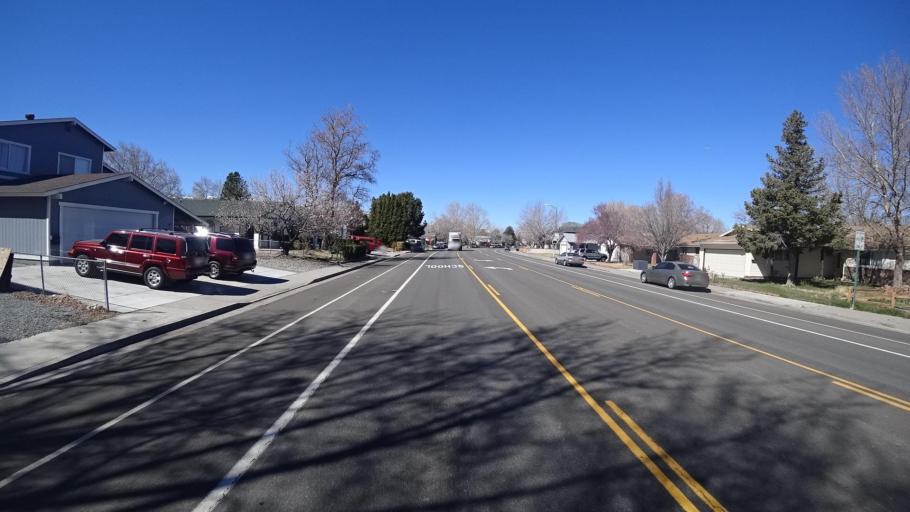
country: US
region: Nevada
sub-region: Washoe County
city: Sparks
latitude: 39.4860
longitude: -119.7539
